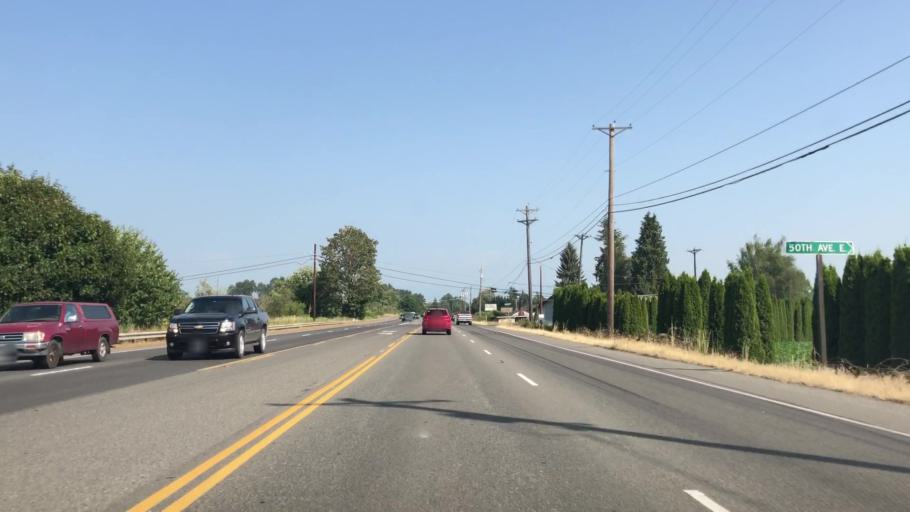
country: US
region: Washington
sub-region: Pierce County
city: Fife
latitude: 47.2245
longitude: -122.3635
